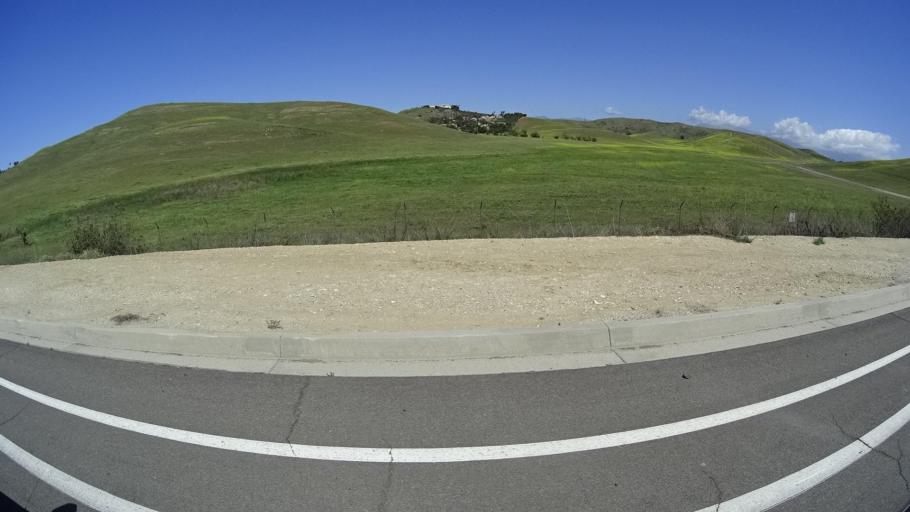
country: US
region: California
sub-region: San Bernardino County
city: Chino Hills
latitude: 33.9975
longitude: -117.7836
